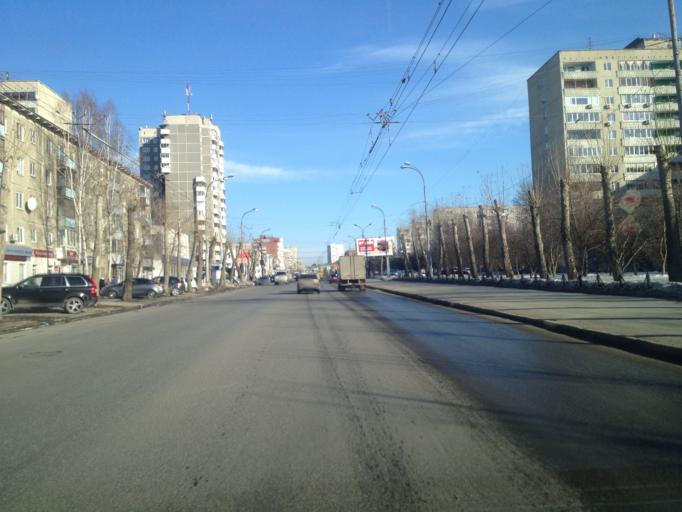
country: RU
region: Sverdlovsk
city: Shirokaya Rechka
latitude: 56.8314
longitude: 60.5408
